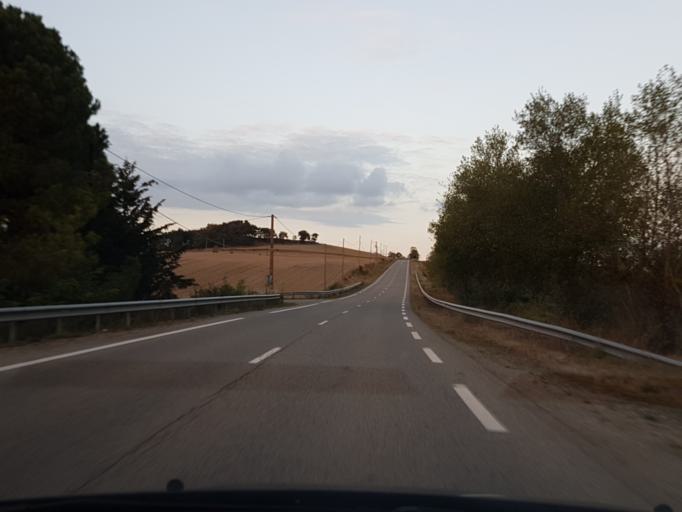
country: FR
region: Midi-Pyrenees
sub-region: Departement de l'Ariege
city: Mirepoix
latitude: 43.1563
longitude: 1.9820
